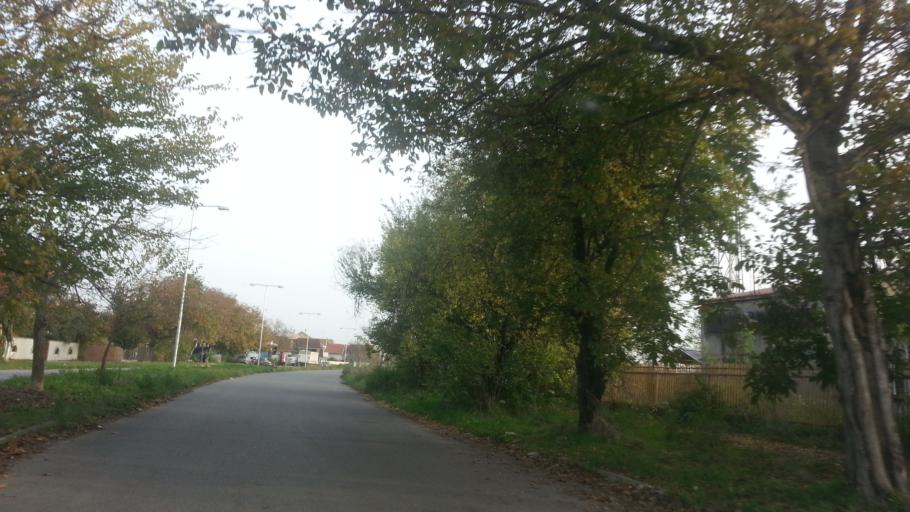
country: RS
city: Novi Banovci
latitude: 44.8988
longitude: 20.2786
